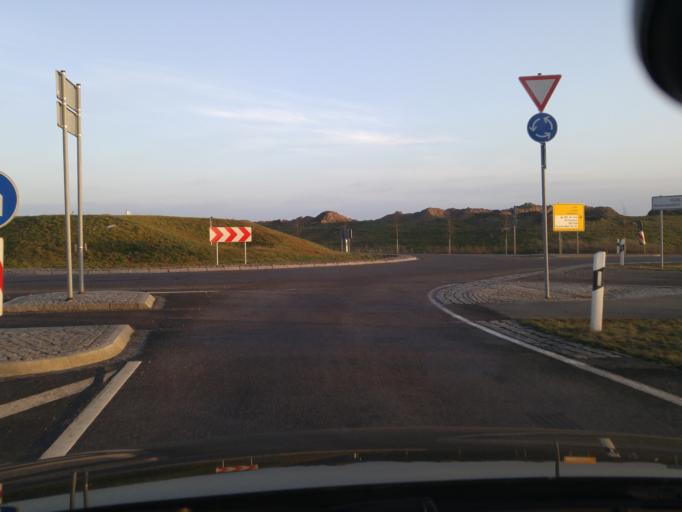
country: DE
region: Saxony
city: Zwochau
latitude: 51.4146
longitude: 12.2786
